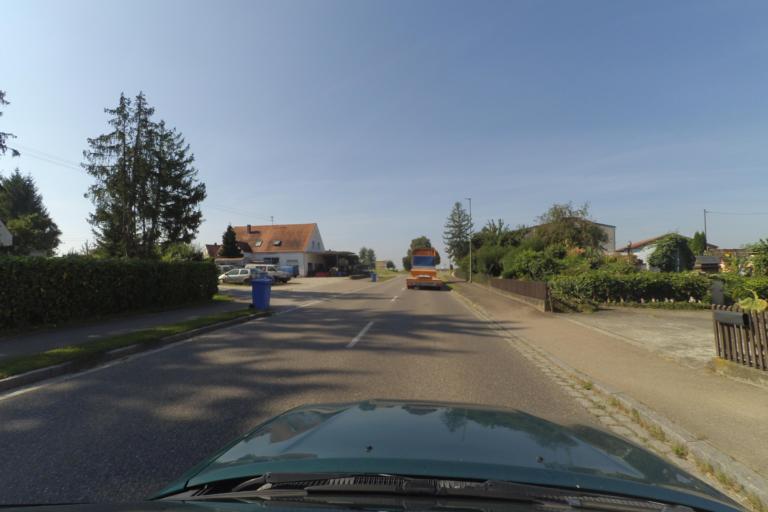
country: DE
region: Bavaria
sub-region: Swabia
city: Schwenningen
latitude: 48.6538
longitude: 10.6412
